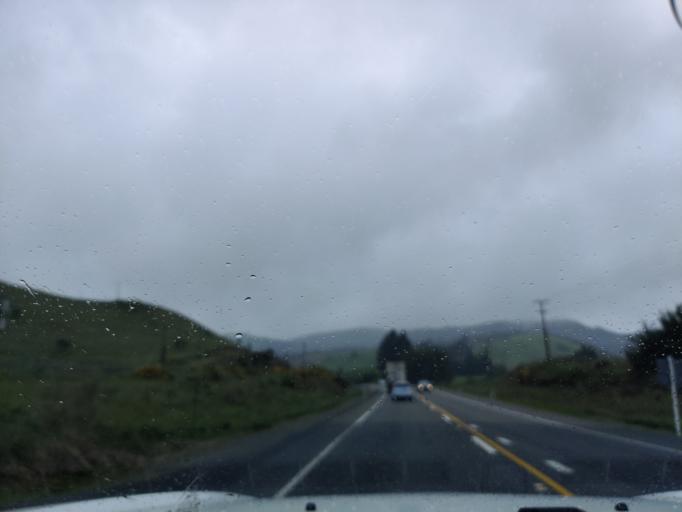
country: NZ
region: Manawatu-Wanganui
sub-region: Ruapehu District
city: Waiouru
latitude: -39.5694
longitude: 175.7043
